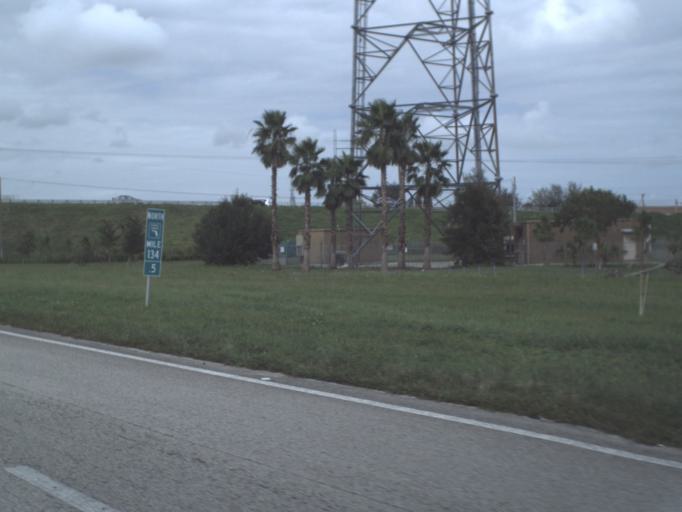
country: US
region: Florida
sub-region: Martin County
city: Palm City
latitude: 27.1602
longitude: -80.3037
